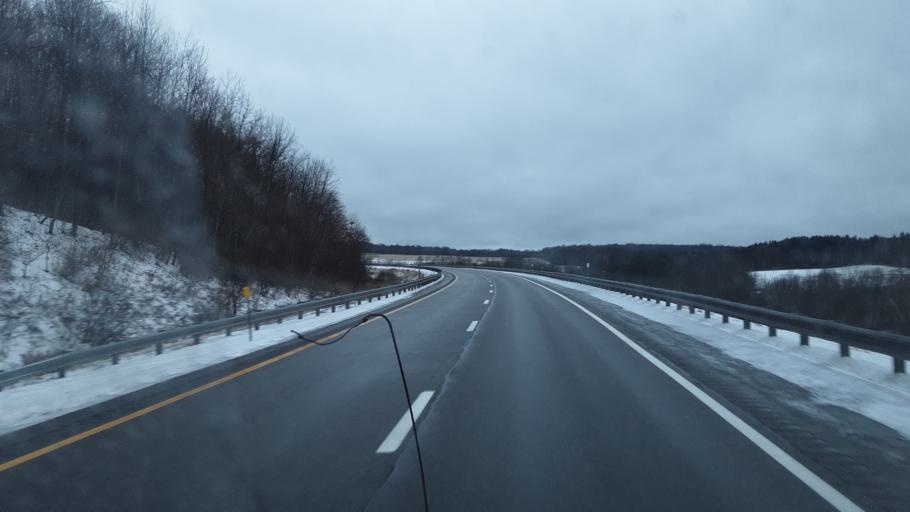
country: US
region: New York
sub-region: Allegany County
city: Alfred
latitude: 42.3171
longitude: -77.8492
